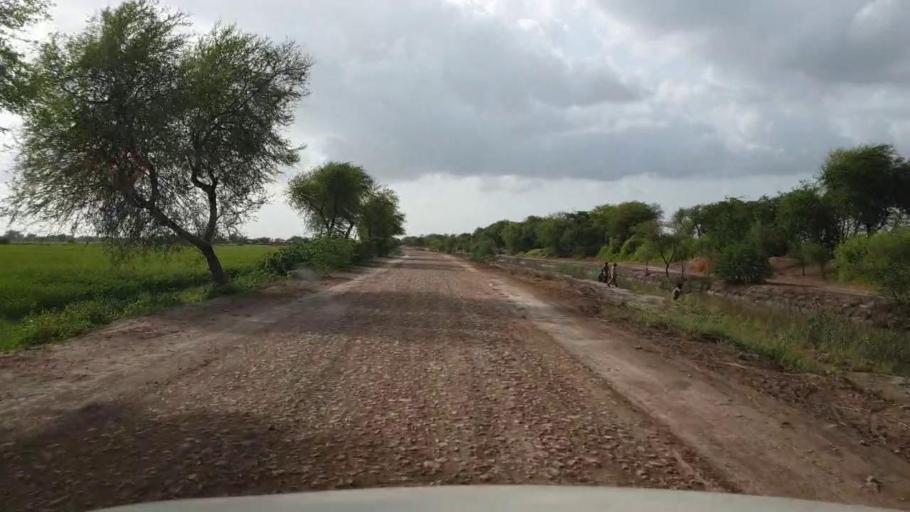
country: PK
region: Sindh
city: Kario
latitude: 24.7861
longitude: 68.5843
